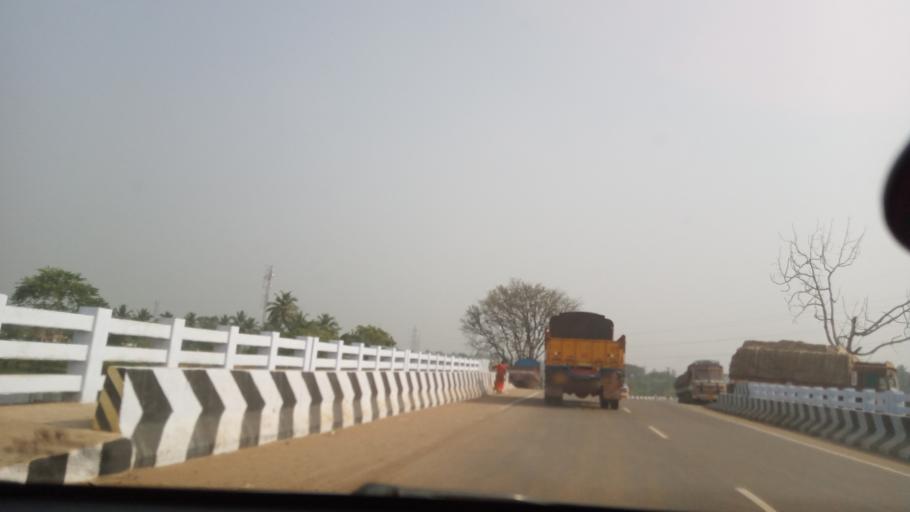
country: IN
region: Tamil Nadu
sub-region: Erode
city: Sathyamangalam
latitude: 11.4492
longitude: 77.2126
